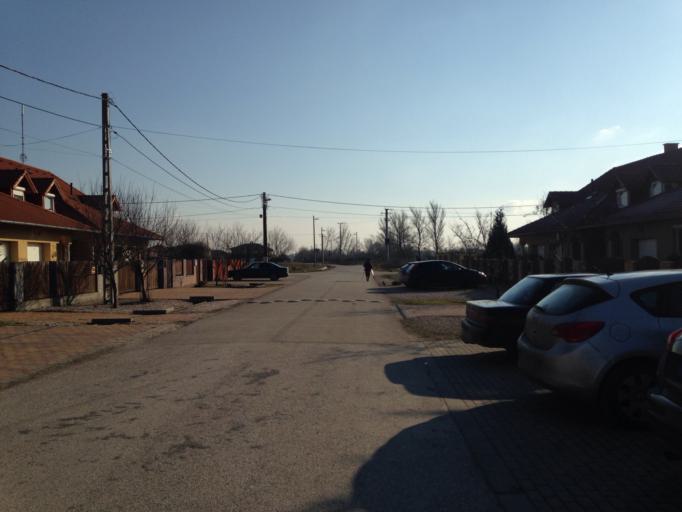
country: HU
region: Pest
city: Dunaharaszti
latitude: 47.3426
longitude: 19.0996
